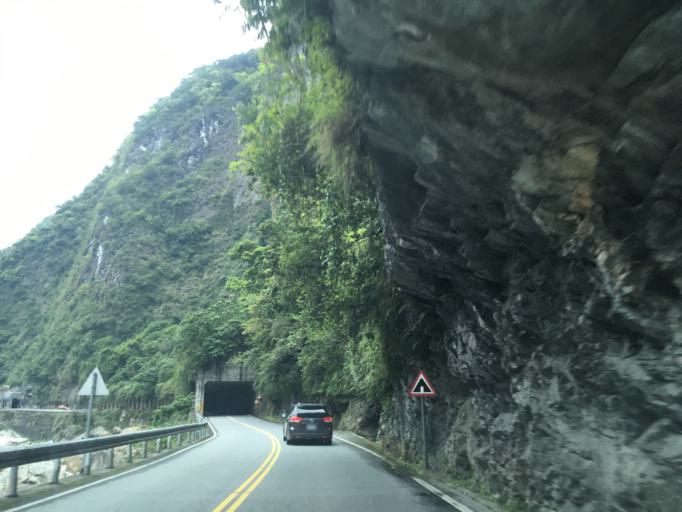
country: TW
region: Taiwan
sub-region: Hualien
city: Hualian
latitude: 24.1701
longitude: 121.6025
